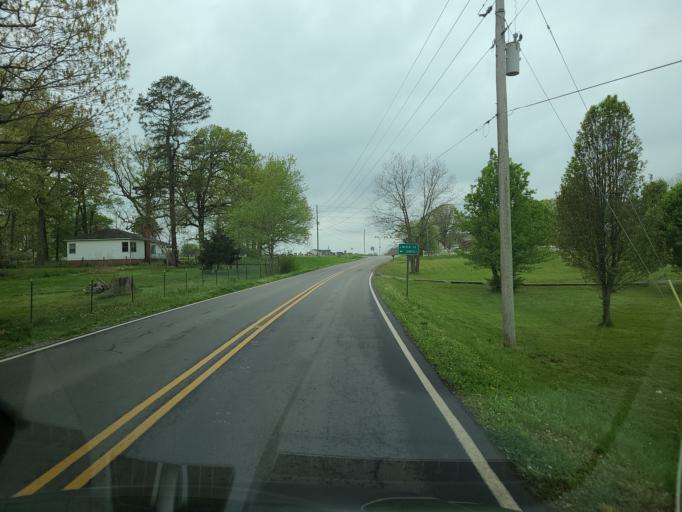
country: US
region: North Carolina
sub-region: Gaston County
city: Cherryville
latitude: 35.4482
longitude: -81.3621
